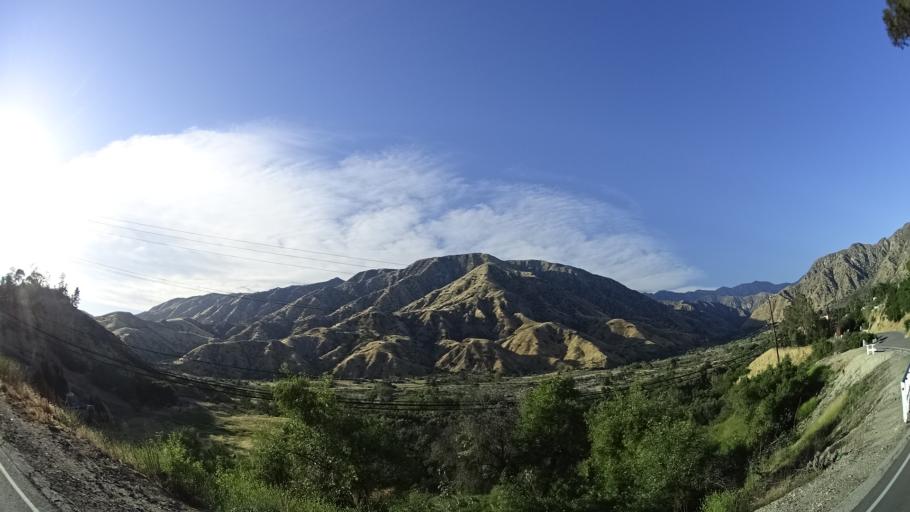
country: US
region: California
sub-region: Los Angeles County
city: La Crescenta-Montrose
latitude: 34.2741
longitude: -118.3024
